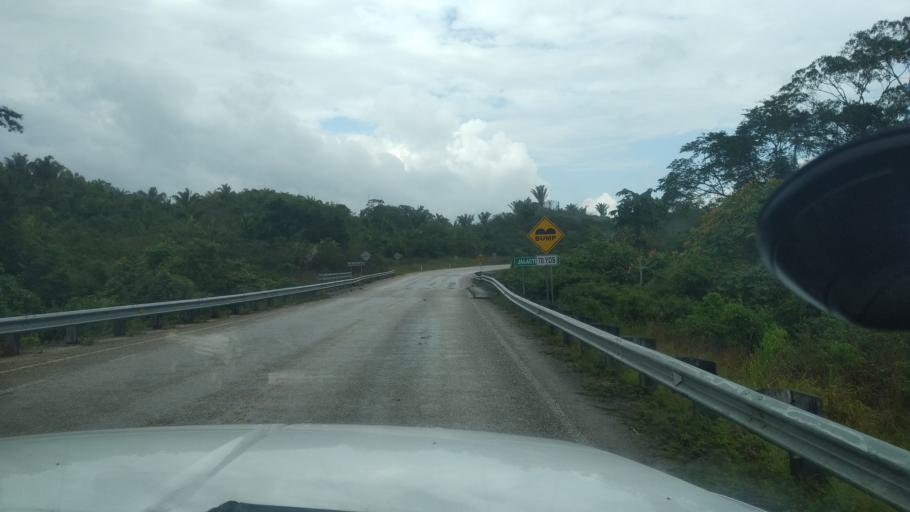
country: GT
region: Peten
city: San Luis
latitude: 16.1897
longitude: -89.1873
